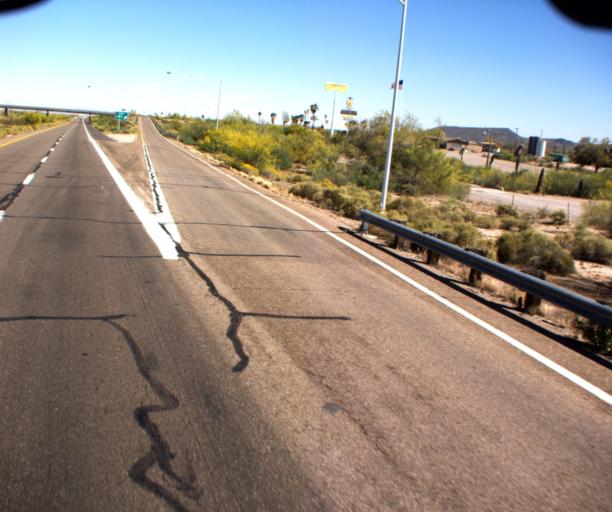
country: US
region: Arizona
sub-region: Pinal County
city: Maricopa
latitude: 32.8346
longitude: -112.1371
